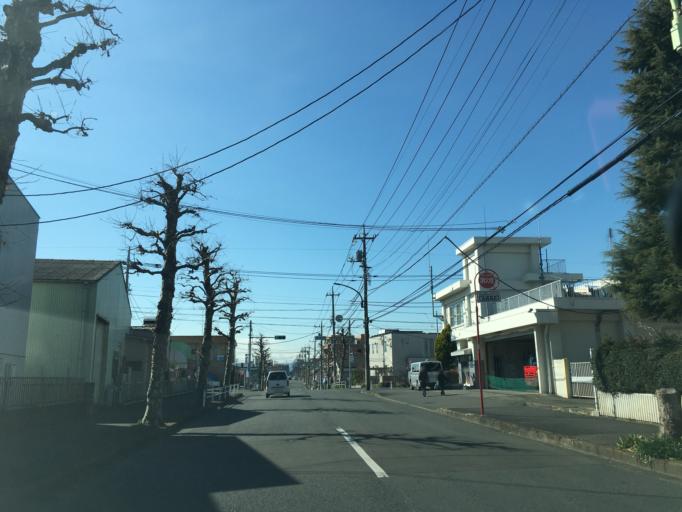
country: JP
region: Tokyo
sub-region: Machida-shi
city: Machida
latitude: 35.5768
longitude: 139.4196
